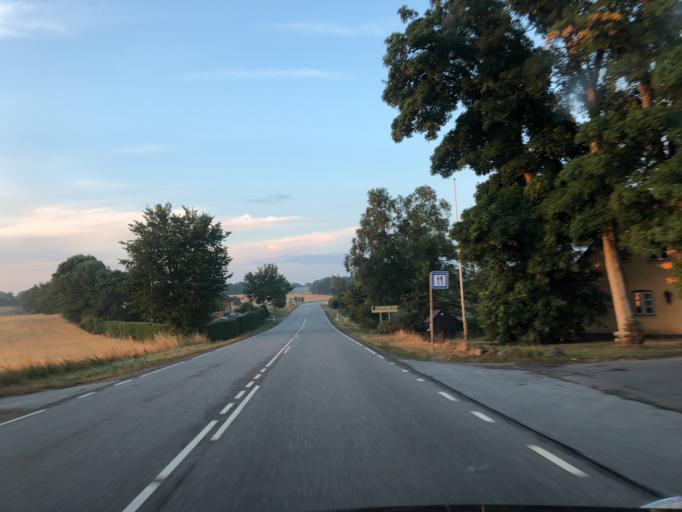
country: DK
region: Zealand
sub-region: Soro Kommune
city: Stenlille
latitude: 55.5992
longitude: 11.6570
